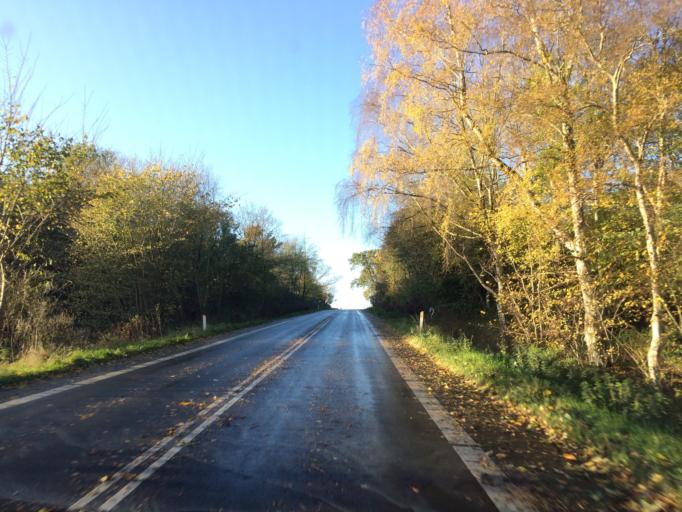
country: DK
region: South Denmark
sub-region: Kolding Kommune
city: Sonder Bjert
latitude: 55.5166
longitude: 9.5382
